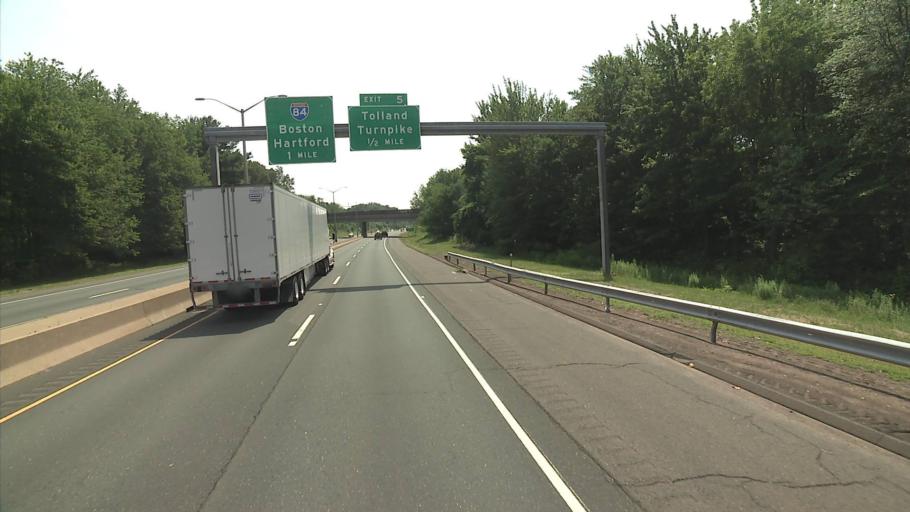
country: US
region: Connecticut
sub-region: Hartford County
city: East Hartford
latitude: 41.8014
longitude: -72.5847
